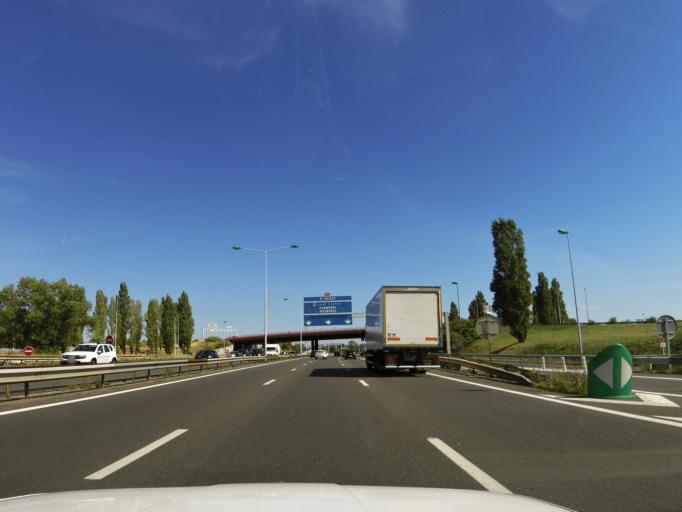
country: FR
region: Rhone-Alpes
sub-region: Departement du Rhone
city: Bron
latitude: 45.7251
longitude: 4.9213
